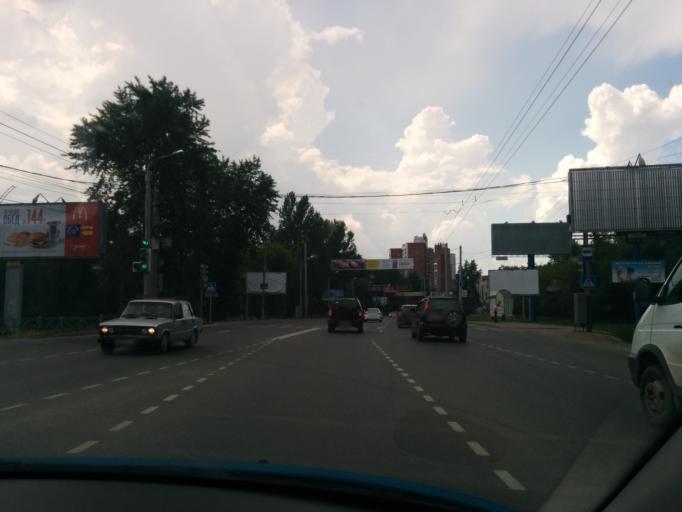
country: RU
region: Perm
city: Kondratovo
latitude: 57.9825
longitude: 56.1798
